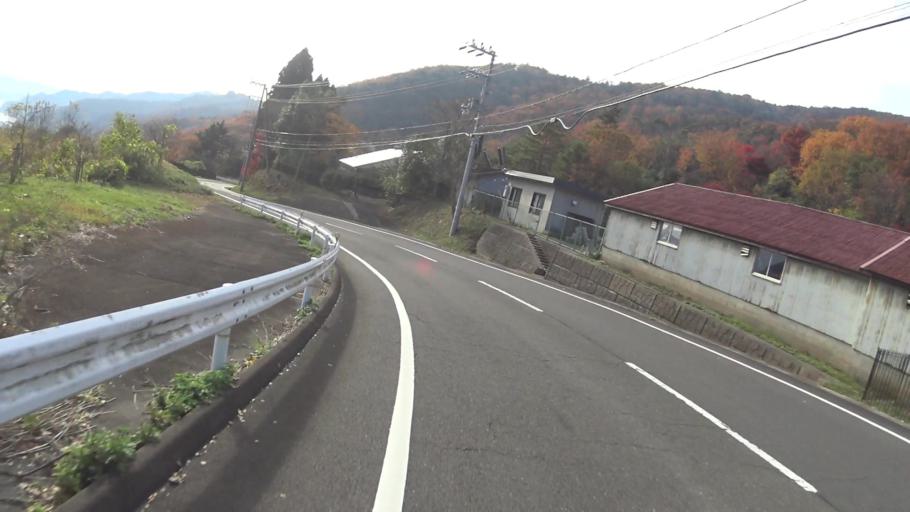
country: JP
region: Kyoto
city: Maizuru
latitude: 35.5347
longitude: 135.3959
